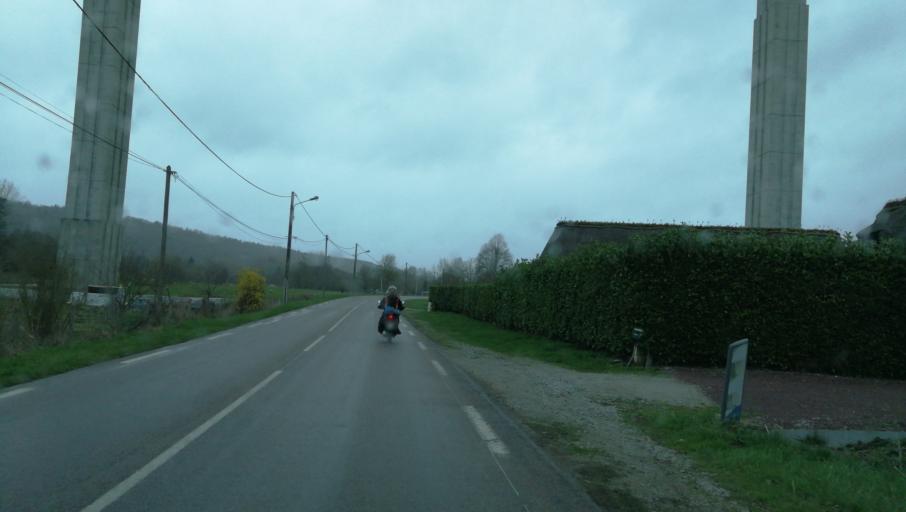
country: FR
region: Haute-Normandie
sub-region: Departement de l'Eure
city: Brionne
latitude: 49.1637
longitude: 0.7252
